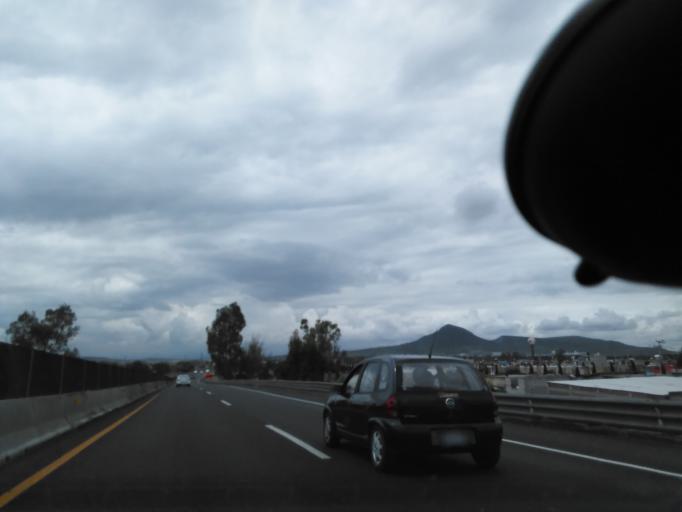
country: MX
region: Mexico
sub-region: Huehuetoca
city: Casa Nueva
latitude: 19.8200
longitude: -99.2051
